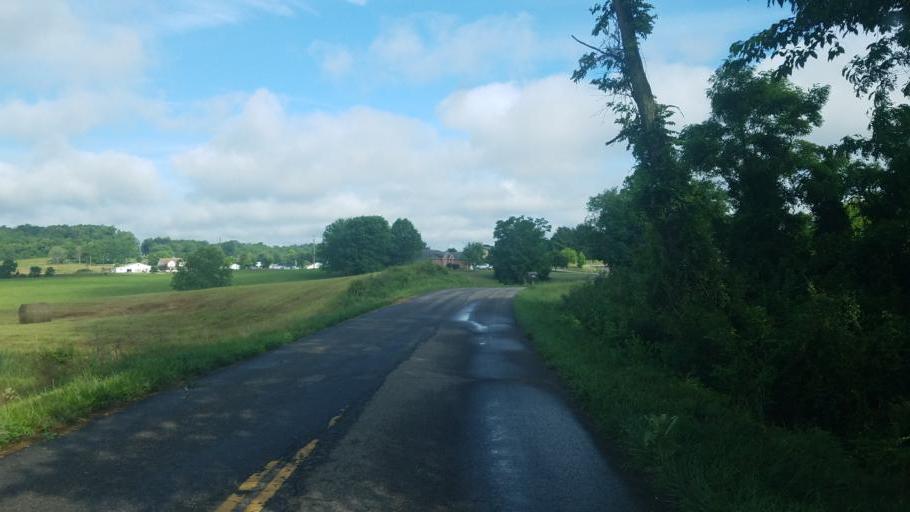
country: US
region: Ohio
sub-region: Gallia County
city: Gallipolis
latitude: 38.7724
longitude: -82.3752
